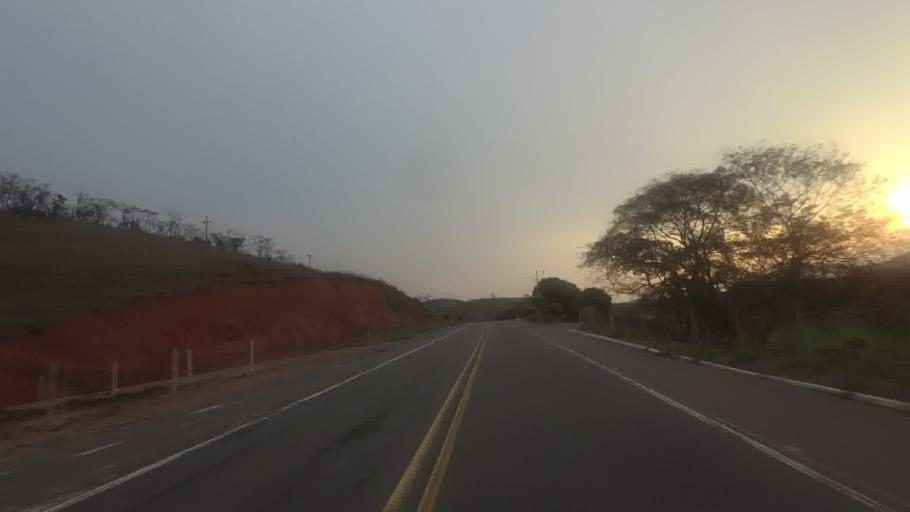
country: BR
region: Minas Gerais
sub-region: Recreio
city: Recreio
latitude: -21.7389
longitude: -42.4521
